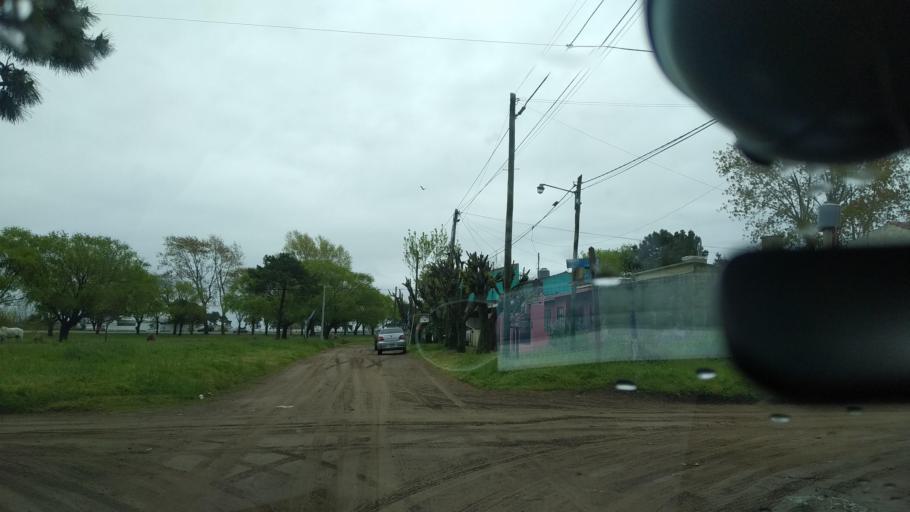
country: AR
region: Buenos Aires
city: Mar del Tuyu
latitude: -36.5307
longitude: -56.7144
